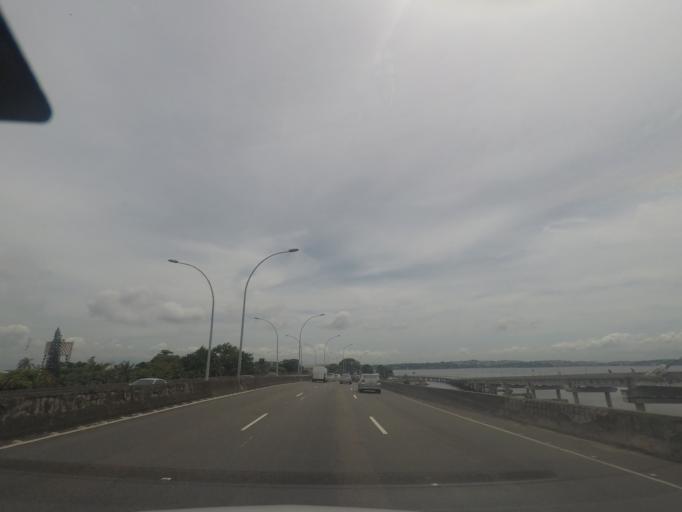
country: BR
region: Rio de Janeiro
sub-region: Rio De Janeiro
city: Rio de Janeiro
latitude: -22.8348
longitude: -43.2403
